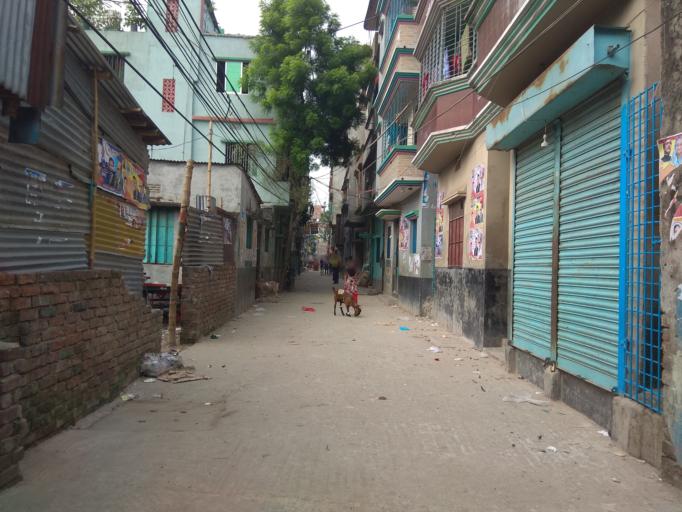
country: BD
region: Dhaka
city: Azimpur
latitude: 23.7203
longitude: 90.3757
